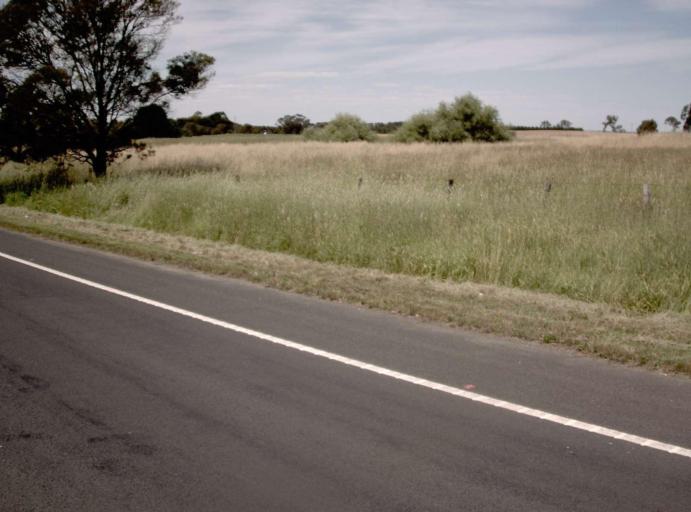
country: AU
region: Victoria
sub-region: Latrobe
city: Traralgon
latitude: -38.1588
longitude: 146.7083
